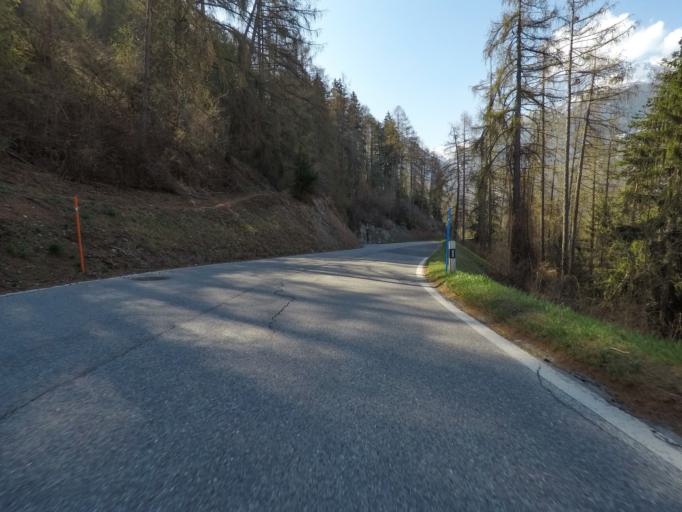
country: CH
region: Valais
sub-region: Conthey District
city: Basse-Nendaz
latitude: 46.1920
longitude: 7.3315
